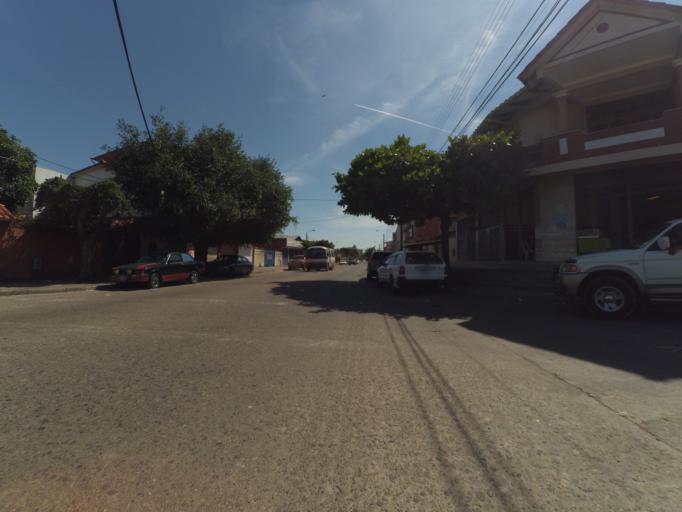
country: BO
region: Santa Cruz
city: Santa Cruz de la Sierra
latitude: -17.8043
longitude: -63.1943
